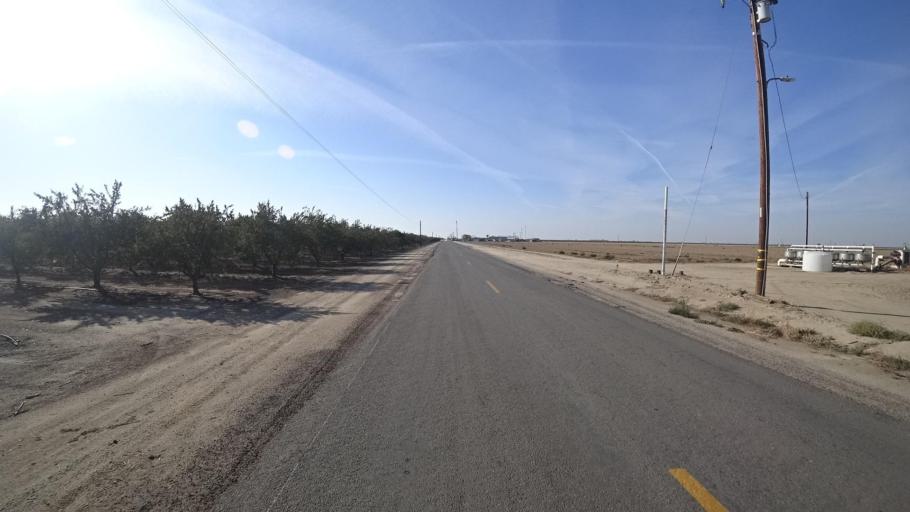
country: US
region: California
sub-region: Kern County
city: McFarland
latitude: 35.7033
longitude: -119.2807
